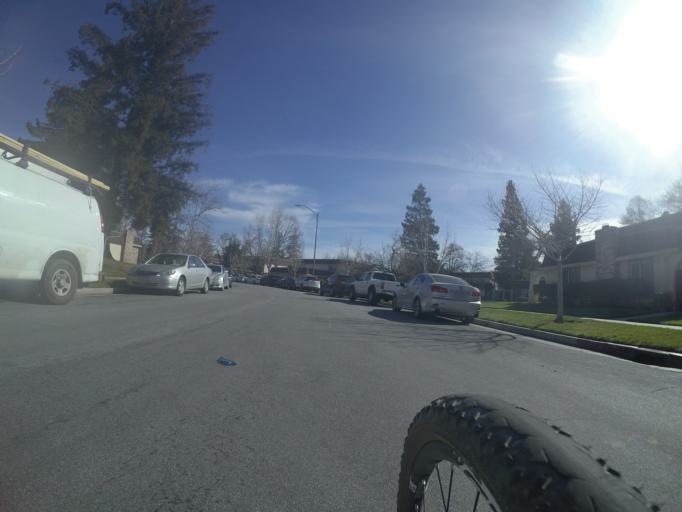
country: US
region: California
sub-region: Santa Clara County
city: Milpitas
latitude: 37.4104
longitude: -121.8646
